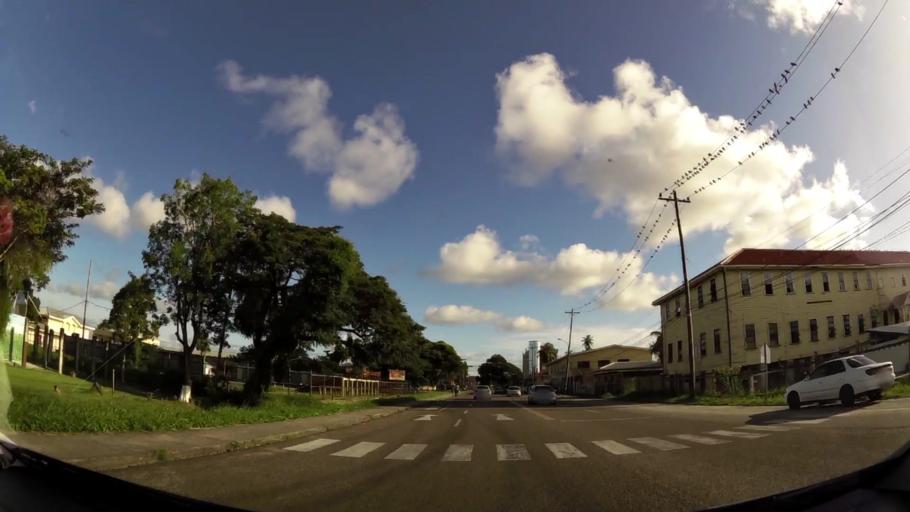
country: GY
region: Demerara-Mahaica
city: Georgetown
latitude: 6.8207
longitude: -58.1578
